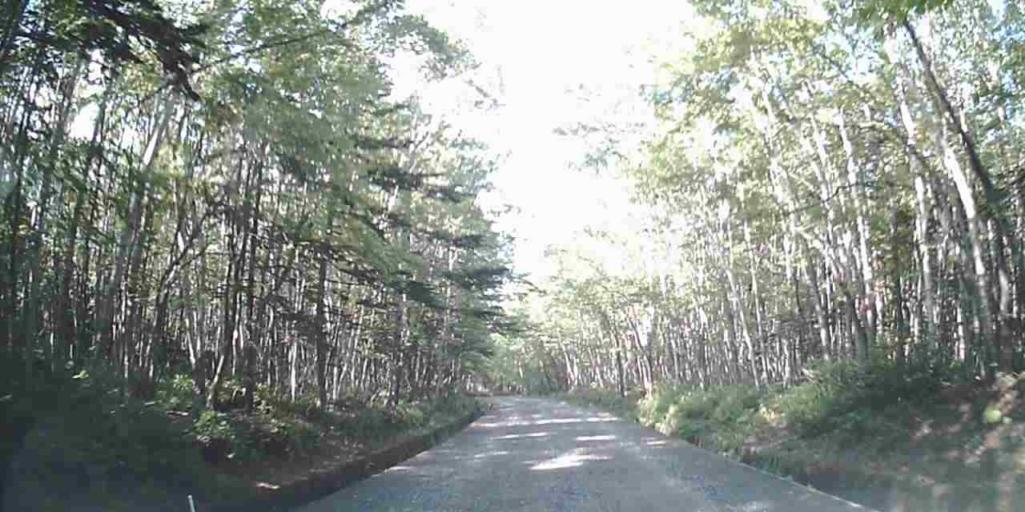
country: JP
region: Hokkaido
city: Shiraoi
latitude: 42.7083
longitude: 141.3981
